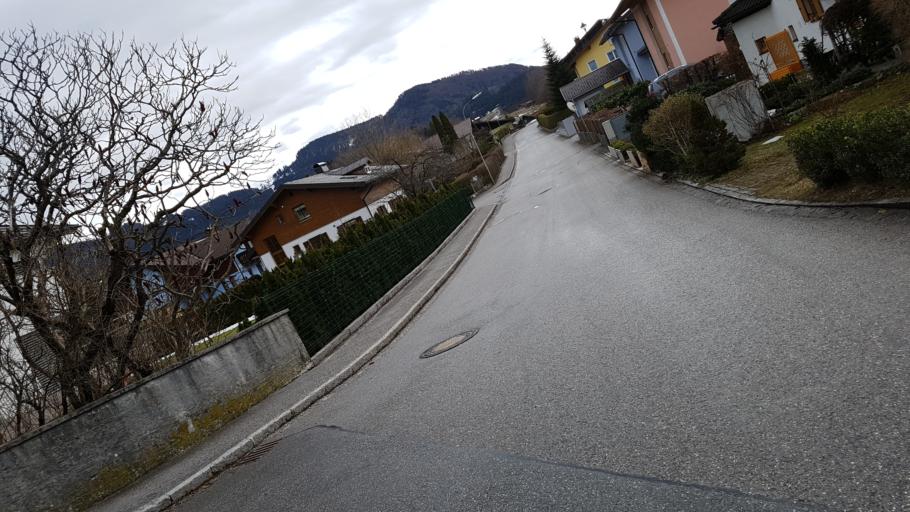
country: AT
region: Salzburg
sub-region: Politischer Bezirk Salzburg-Umgebung
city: Henndorf am Wallersee
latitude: 47.8989
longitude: 13.1831
